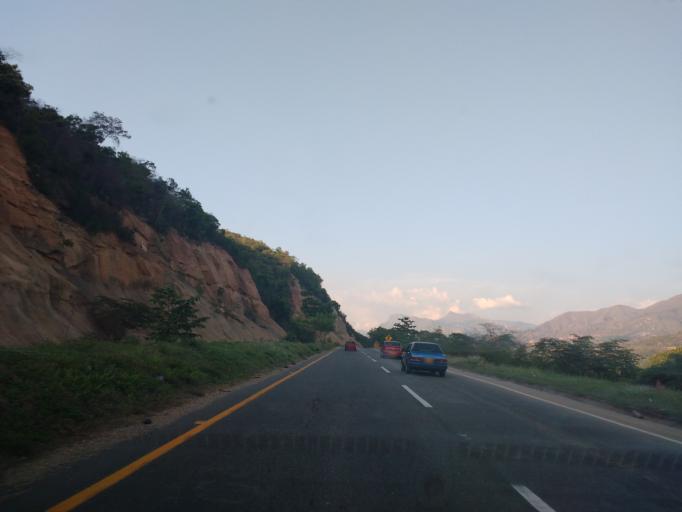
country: CO
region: Tolima
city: Melgar
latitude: 4.2200
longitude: -74.6366
